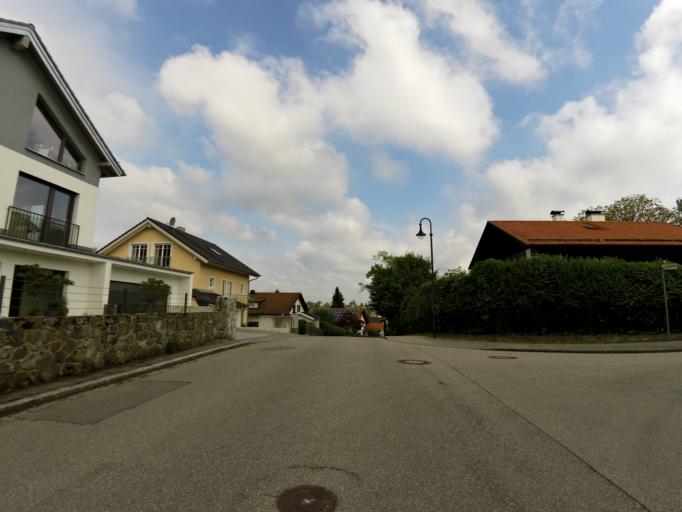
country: DE
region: Bavaria
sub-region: Upper Bavaria
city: Schaftlarn
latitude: 47.9832
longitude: 11.4560
